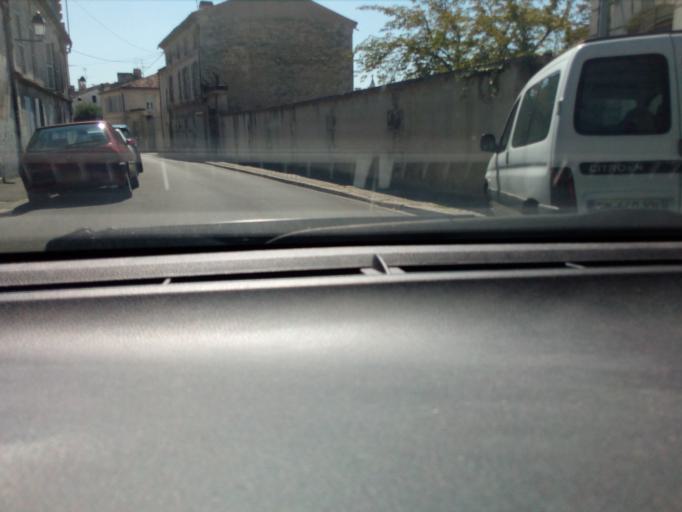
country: FR
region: Poitou-Charentes
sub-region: Departement de la Charente
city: Angouleme
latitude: 45.6588
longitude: 0.1613
